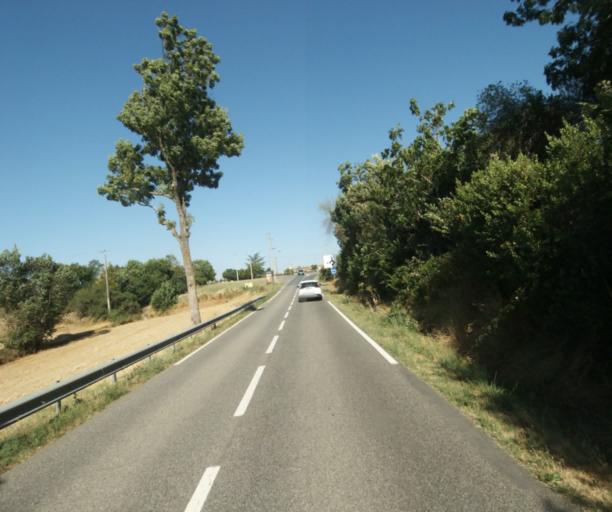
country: FR
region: Midi-Pyrenees
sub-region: Departement de la Haute-Garonne
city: Saint-Felix-Lauragais
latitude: 43.4805
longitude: 1.9179
